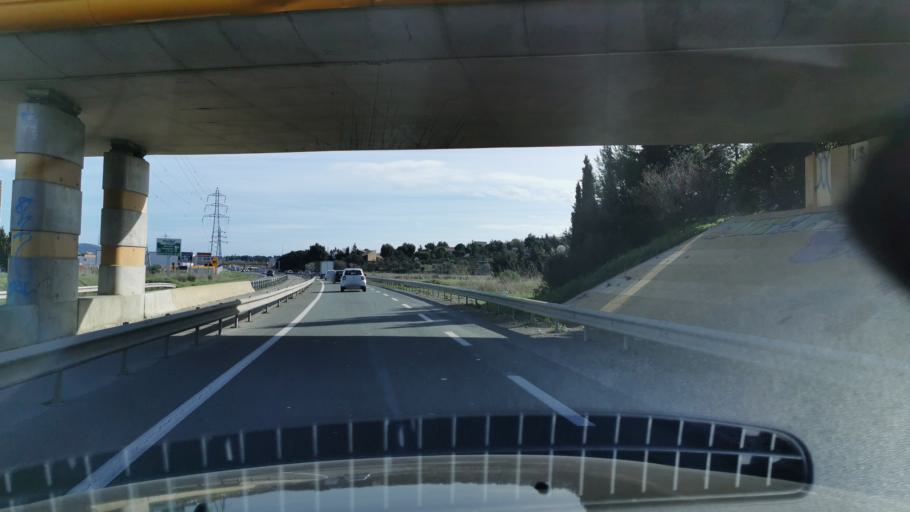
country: FR
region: Languedoc-Roussillon
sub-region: Departement de l'Aude
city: Narbonne
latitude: 43.1719
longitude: 2.9771
